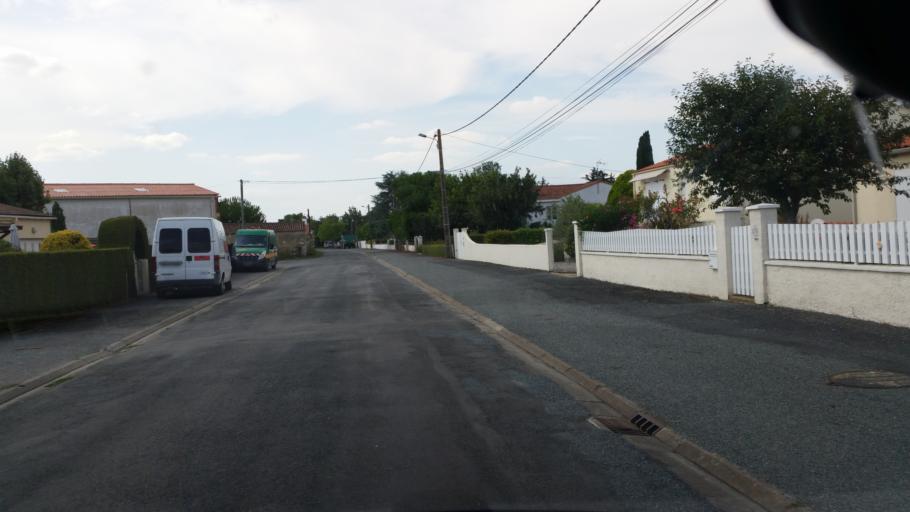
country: FR
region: Poitou-Charentes
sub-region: Departement de la Charente-Maritime
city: Marans
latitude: 46.3059
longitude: -0.9837
